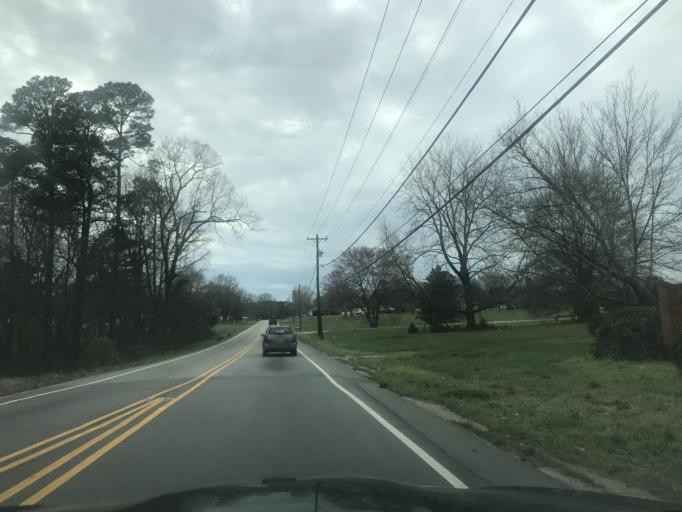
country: US
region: North Carolina
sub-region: Franklin County
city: Franklinton
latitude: 36.1036
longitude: -78.4382
